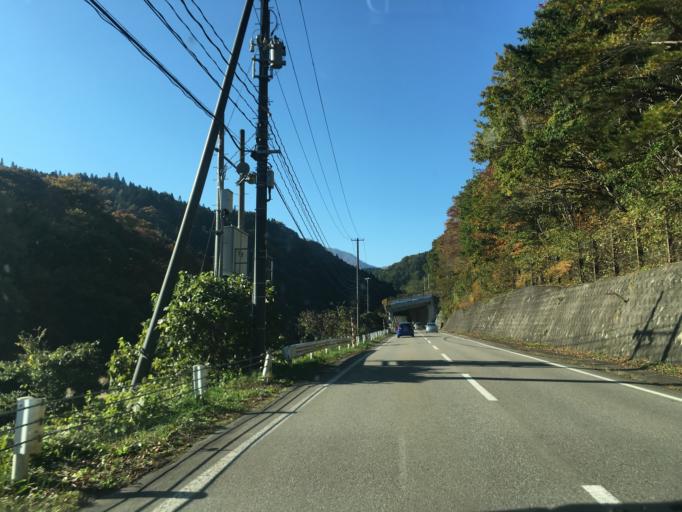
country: JP
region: Fukushima
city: Inawashiro
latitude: 37.3006
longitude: 139.9451
